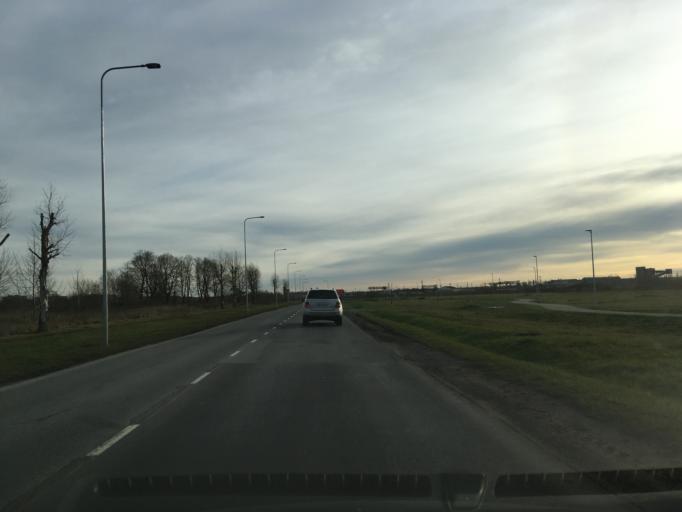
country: EE
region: Ida-Virumaa
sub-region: Narva linn
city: Narva
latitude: 59.3675
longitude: 28.1607
